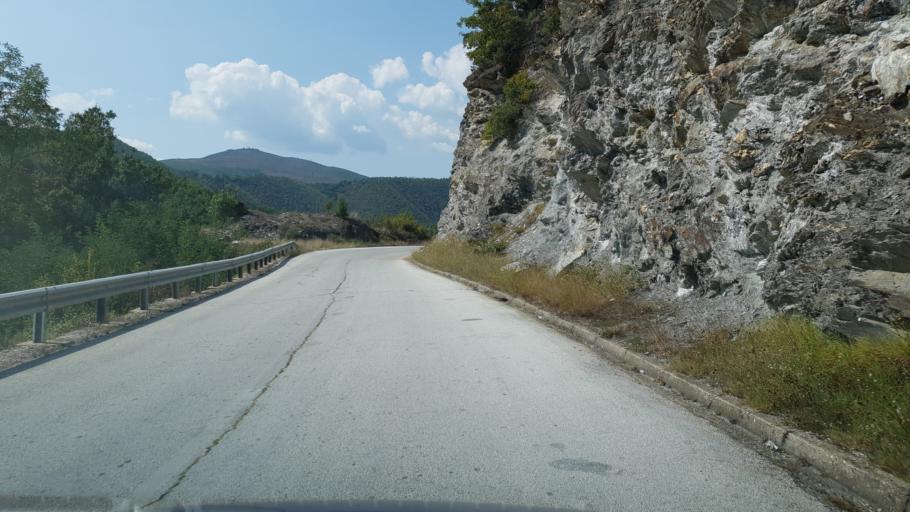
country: MK
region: Makedonski Brod
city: Samokov
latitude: 41.6639
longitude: 21.2254
